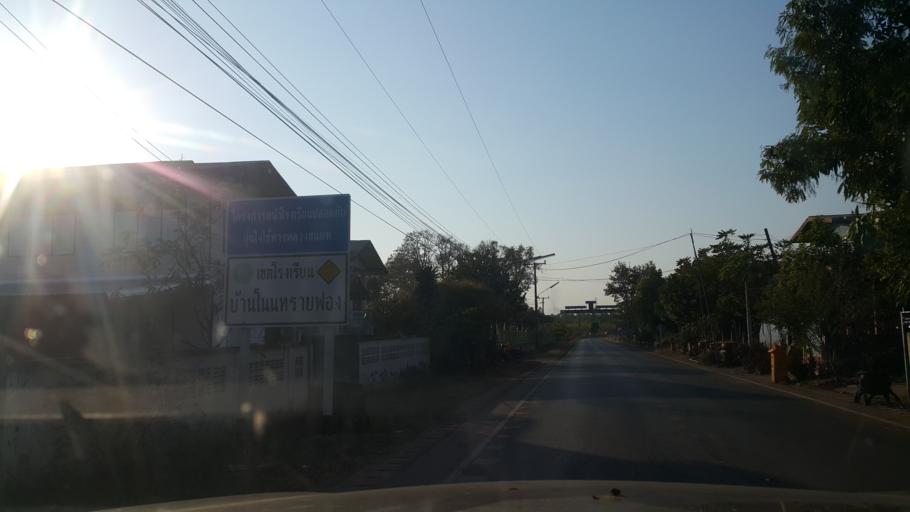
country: TH
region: Changwat Udon Thani
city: Ban Na Muang
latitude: 17.3036
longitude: 102.9452
